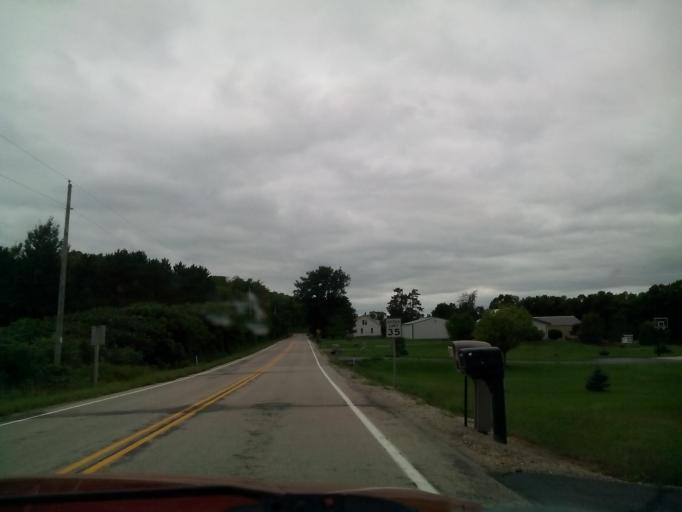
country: US
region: Wisconsin
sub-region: Outagamie County
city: Hortonville
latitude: 44.3506
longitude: -88.6273
